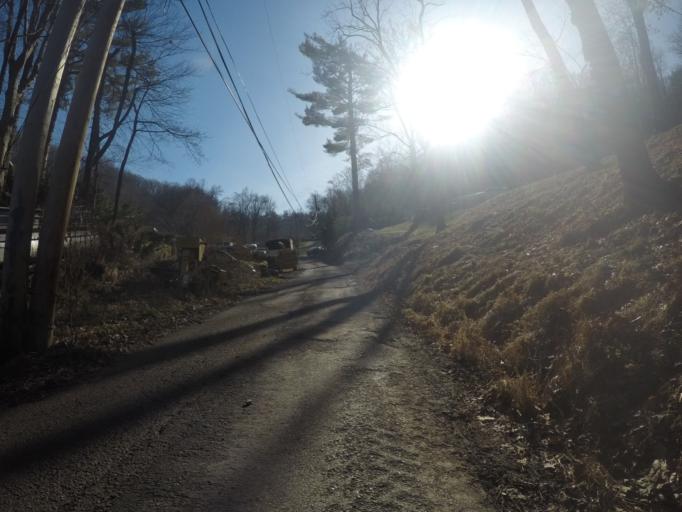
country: US
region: Ohio
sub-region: Lawrence County
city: Burlington
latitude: 38.3946
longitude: -82.4986
